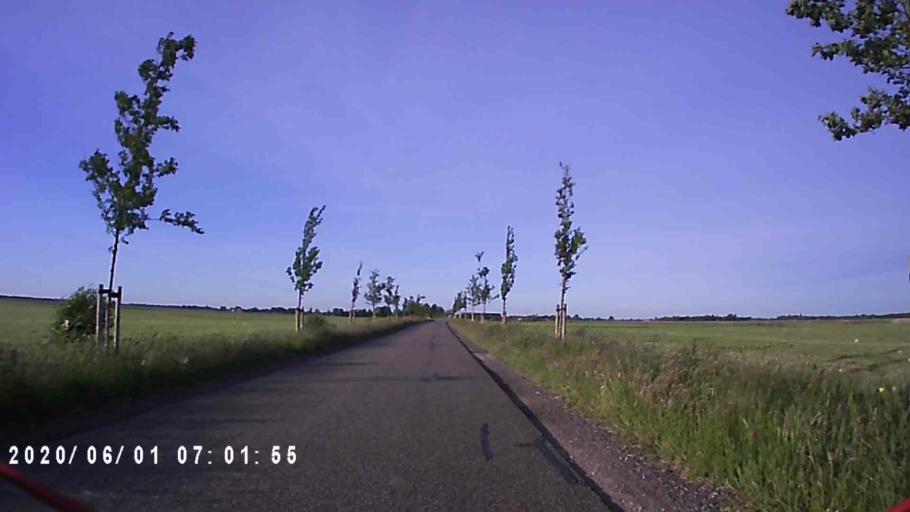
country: NL
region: Friesland
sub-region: Gemeente Kollumerland en Nieuwkruisland
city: Kollumerzwaag
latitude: 53.3133
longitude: 6.0889
